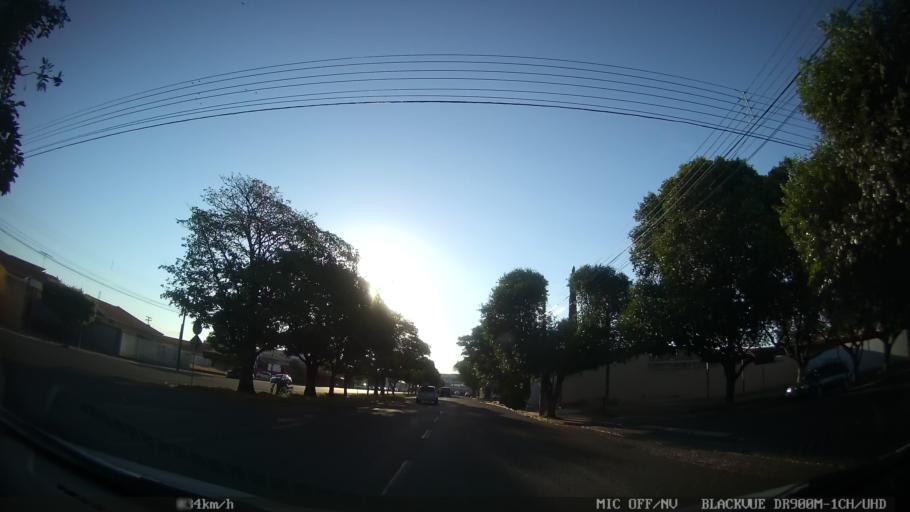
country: BR
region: Sao Paulo
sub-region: Sao Jose Do Rio Preto
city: Sao Jose do Rio Preto
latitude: -20.7927
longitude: -49.3588
